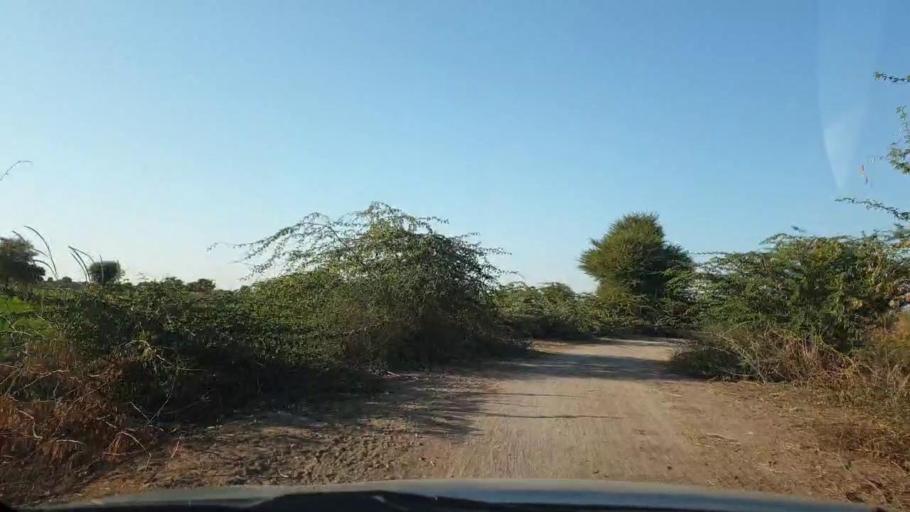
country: PK
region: Sindh
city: Jhol
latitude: 25.9001
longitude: 68.9251
